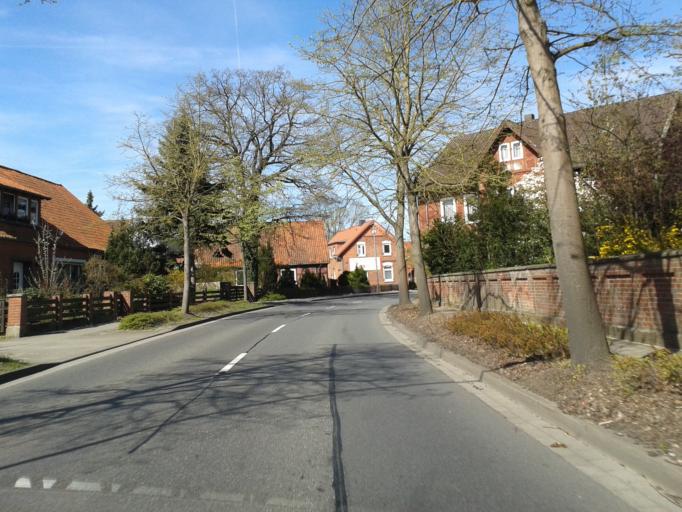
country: DE
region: Lower Saxony
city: Uelzen
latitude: 52.9561
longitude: 10.6049
